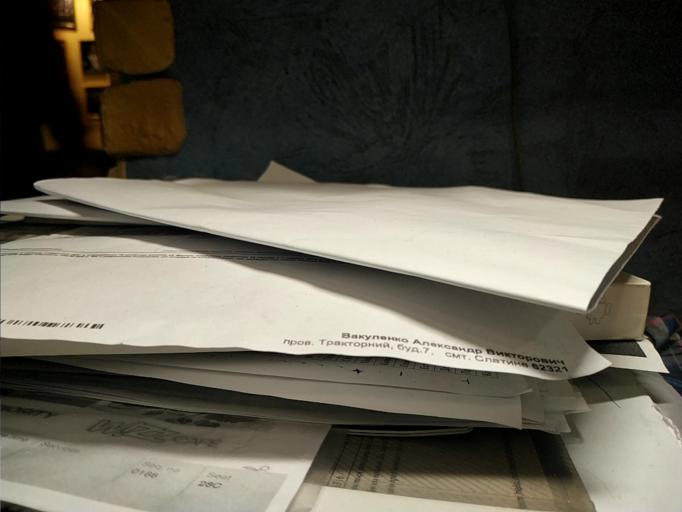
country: RU
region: Tverskaya
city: Zubtsov
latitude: 56.0910
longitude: 34.7409
